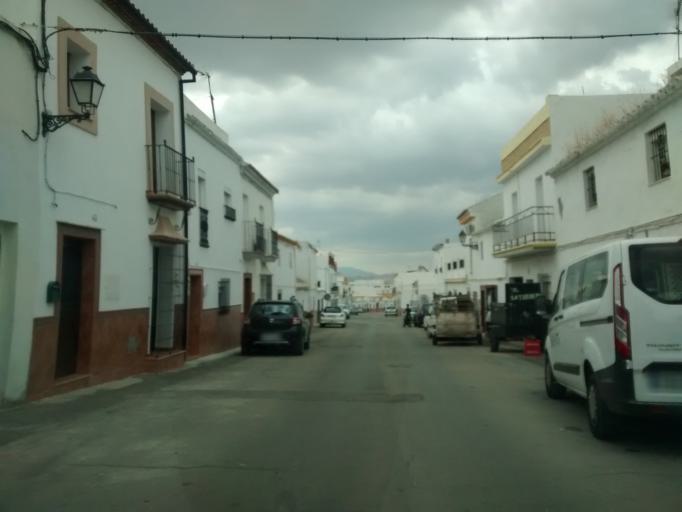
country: ES
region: Andalusia
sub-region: Provincia de Cadiz
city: Bornos
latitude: 36.8163
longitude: -5.7402
